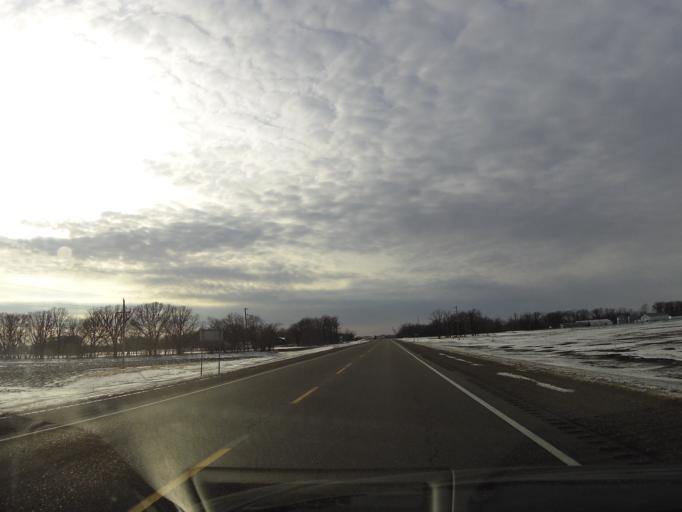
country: US
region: Minnesota
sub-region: Kittson County
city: Hallock
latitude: 48.5729
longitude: -97.1375
